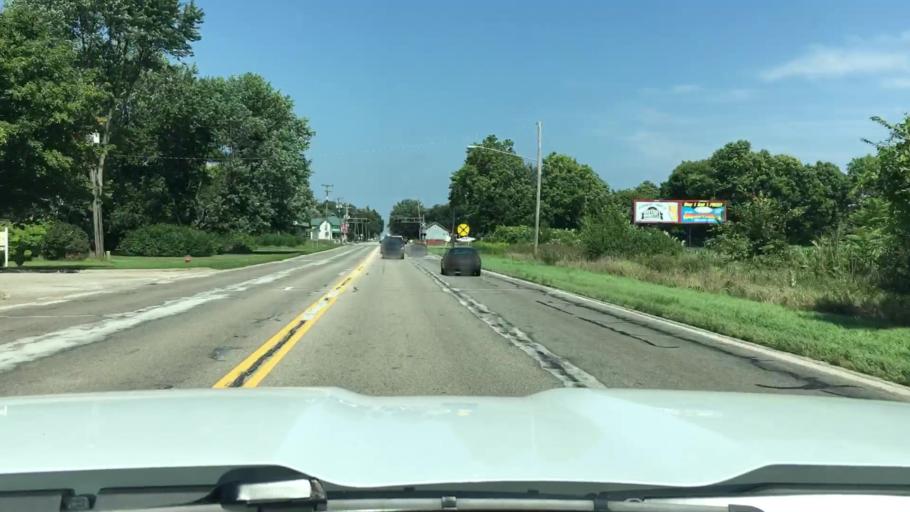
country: US
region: Michigan
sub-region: Kalamazoo County
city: Schoolcraft
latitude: 42.1076
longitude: -85.6371
